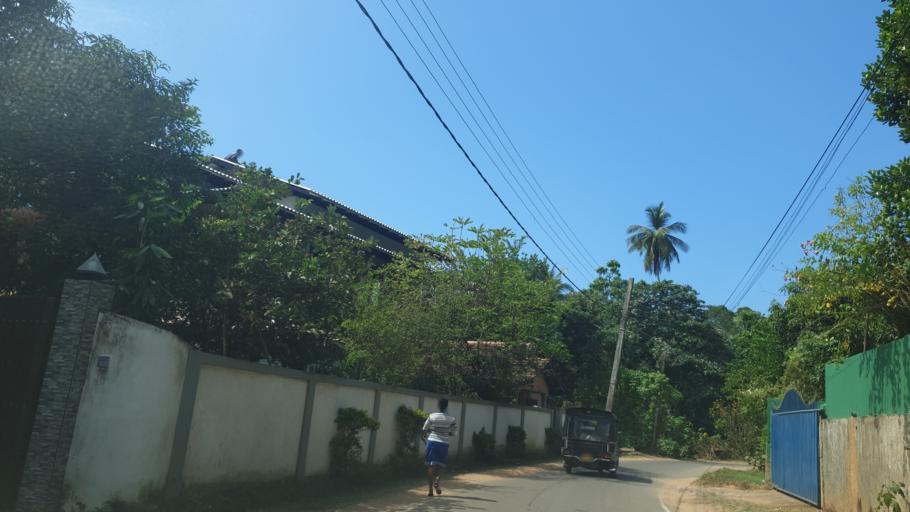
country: LK
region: Southern
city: Tangalla
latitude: 5.9662
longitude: 80.7087
